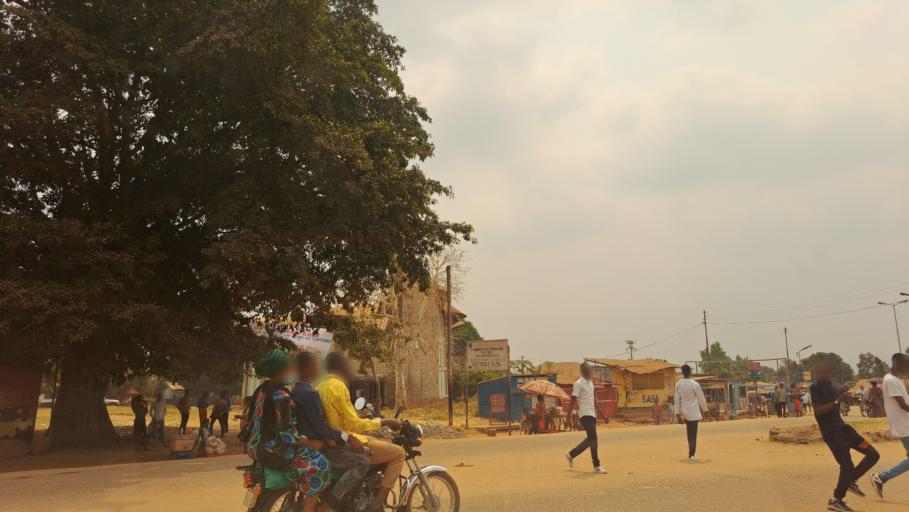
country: CD
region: Kasai-Oriental
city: Mbuji-Mayi
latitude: -6.1073
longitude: 23.5959
